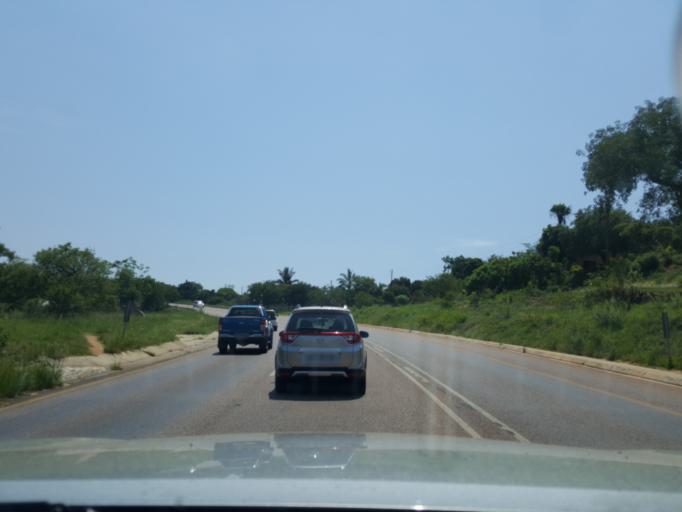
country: ZA
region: Limpopo
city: Thulamahashi
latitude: -24.9738
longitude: 31.1147
